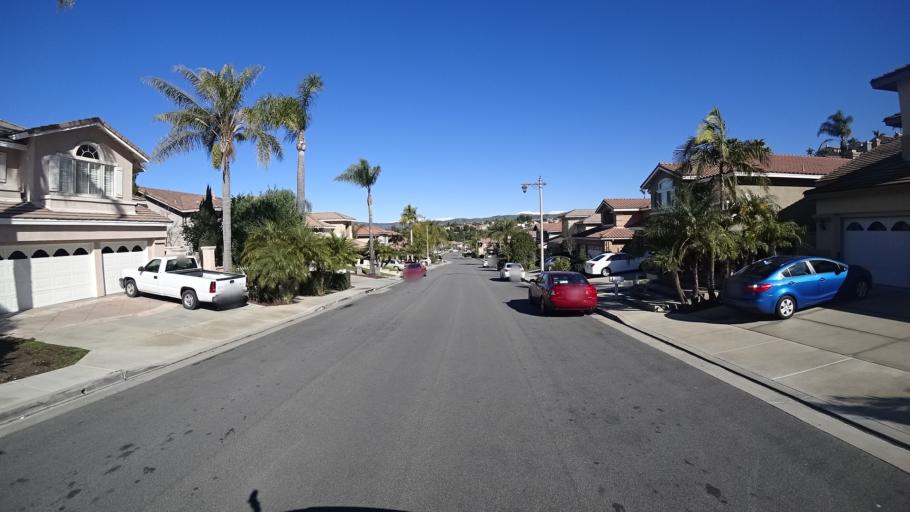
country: US
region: California
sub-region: Orange County
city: Villa Park
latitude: 33.8515
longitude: -117.7517
